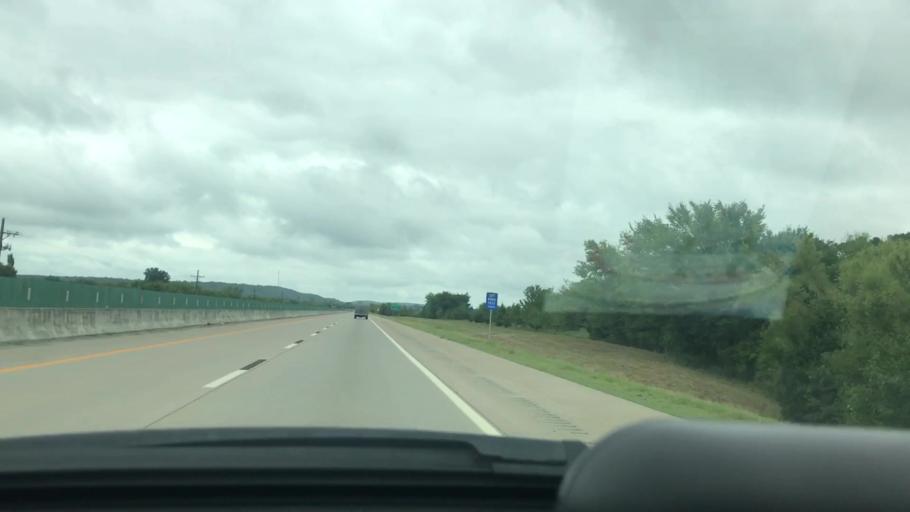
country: US
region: Oklahoma
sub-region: Pittsburg County
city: Krebs
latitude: 35.0372
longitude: -95.7121
